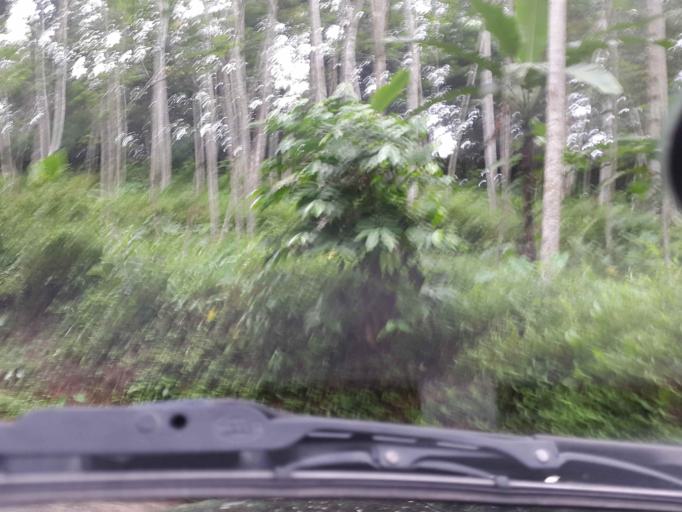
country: ID
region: Central Java
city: Wonosobo
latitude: -7.4261
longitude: 109.8665
